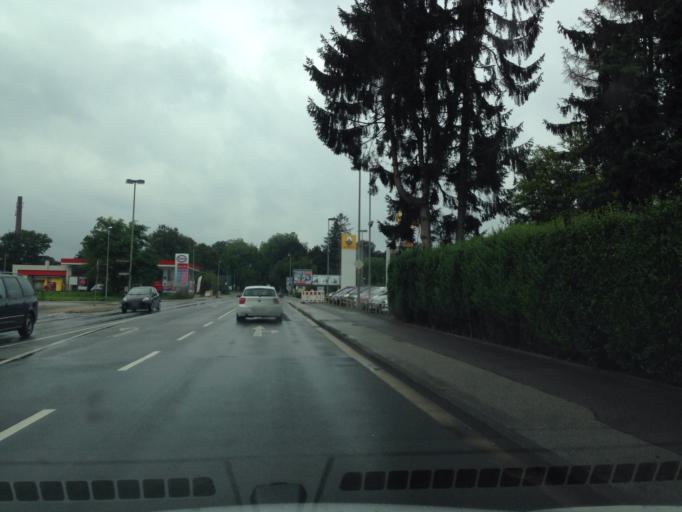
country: DE
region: North Rhine-Westphalia
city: Erkelenz
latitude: 51.0728
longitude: 6.3257
